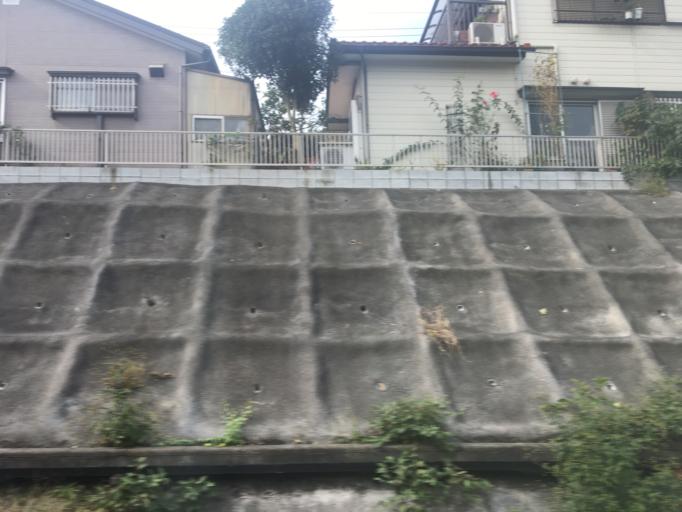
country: JP
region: Saitama
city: Sayama
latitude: 35.8518
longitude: 139.4141
